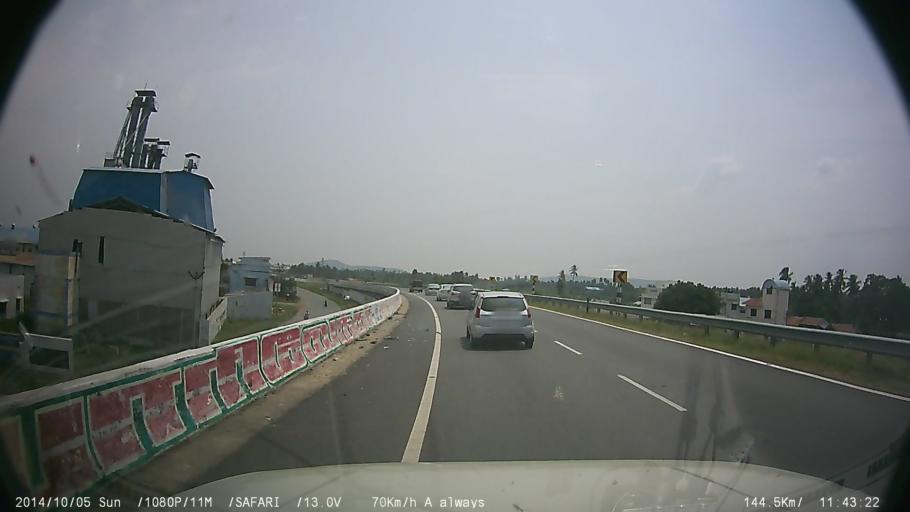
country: IN
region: Tamil Nadu
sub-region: Salem
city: Attur
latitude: 11.5931
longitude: 78.6207
